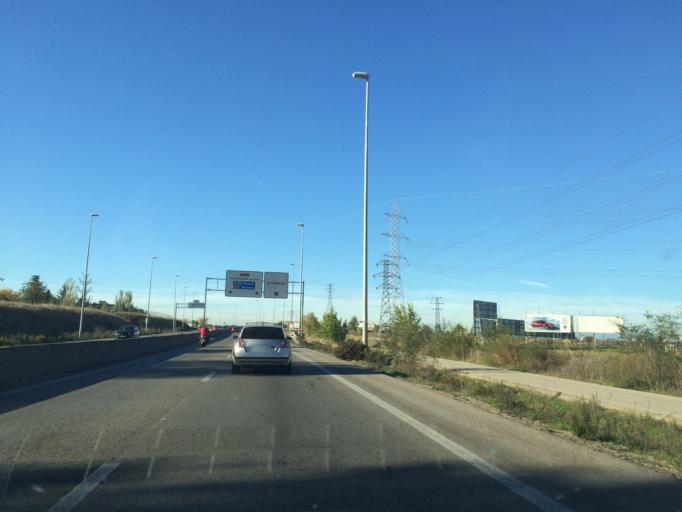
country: ES
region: Madrid
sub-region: Provincia de Madrid
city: Mostoles
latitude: 40.3288
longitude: -3.8500
